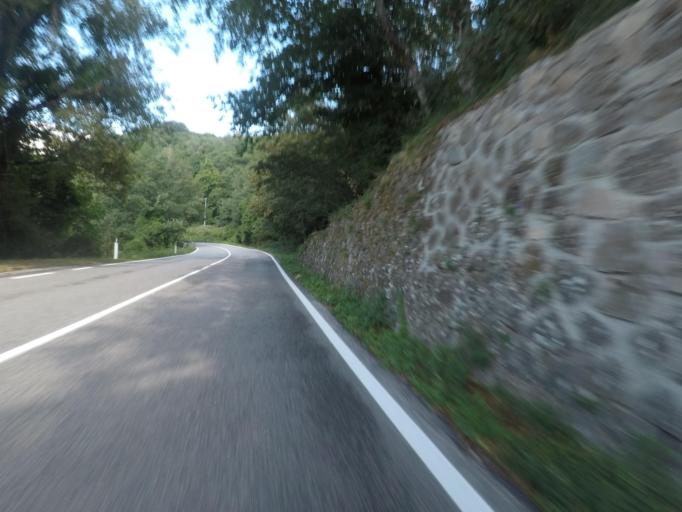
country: IT
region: Tuscany
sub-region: Provincia di Massa-Carrara
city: Comano
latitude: 44.2761
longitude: 10.1849
